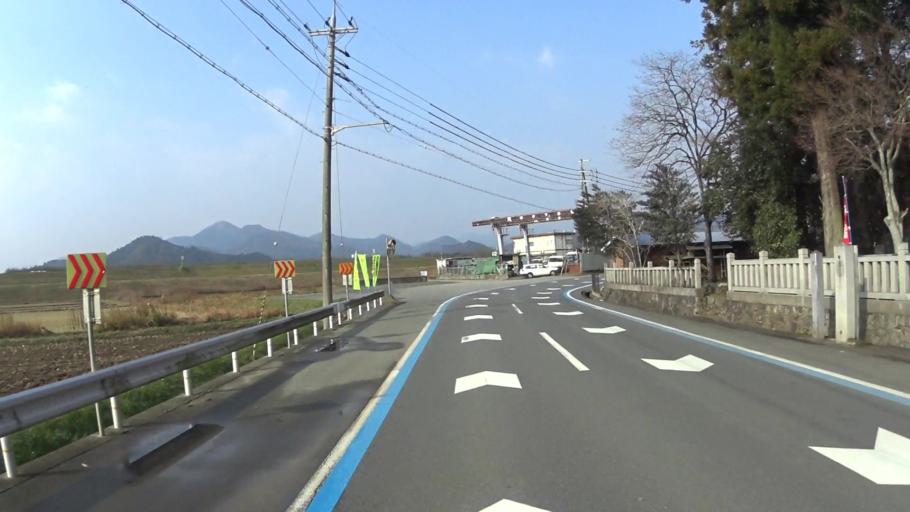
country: JP
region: Kyoto
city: Fukuchiyama
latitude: 35.3195
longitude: 135.1213
